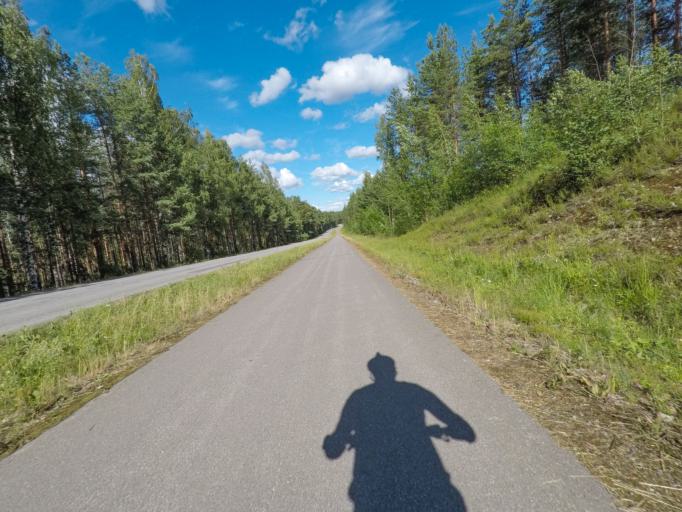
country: FI
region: South Karelia
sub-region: Lappeenranta
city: Joutseno
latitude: 61.1505
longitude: 28.5577
